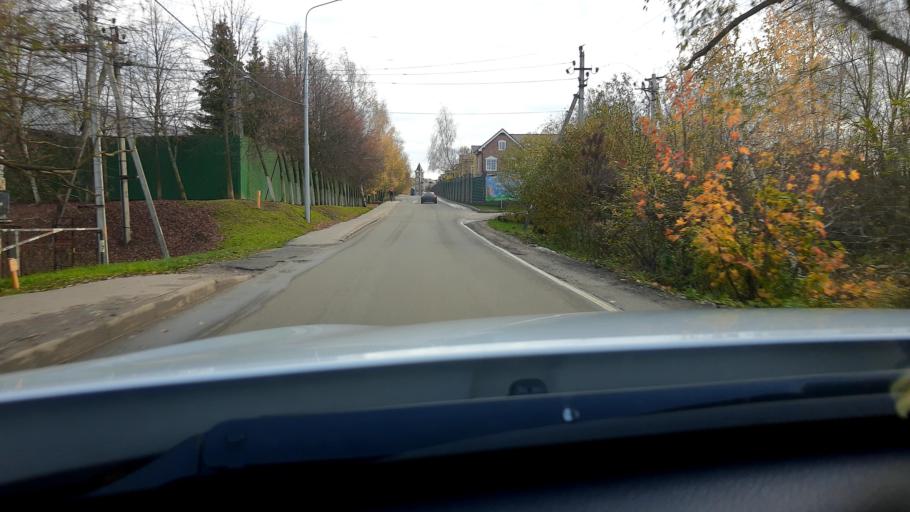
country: RU
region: Moskovskaya
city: Kokoshkino
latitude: 55.5282
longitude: 37.1549
